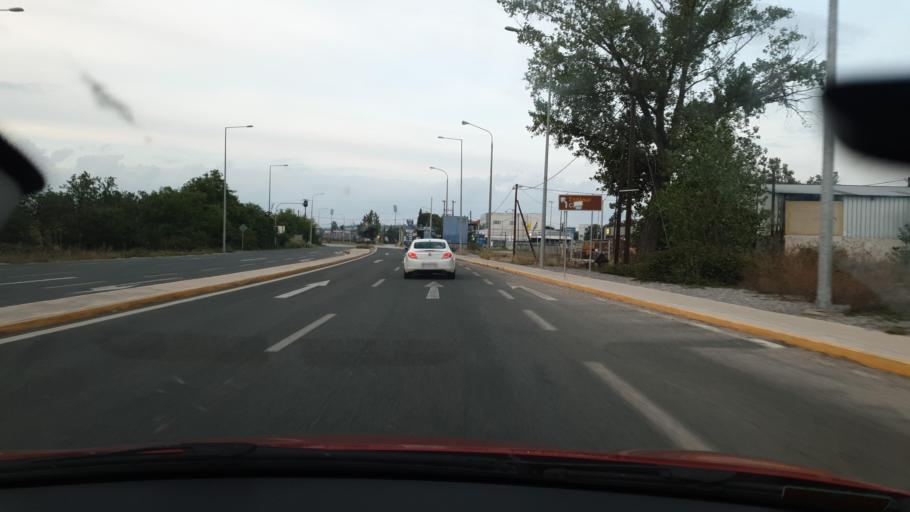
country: GR
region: Central Macedonia
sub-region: Nomos Kilkis
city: Kilkis
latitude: 40.9804
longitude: 22.8625
